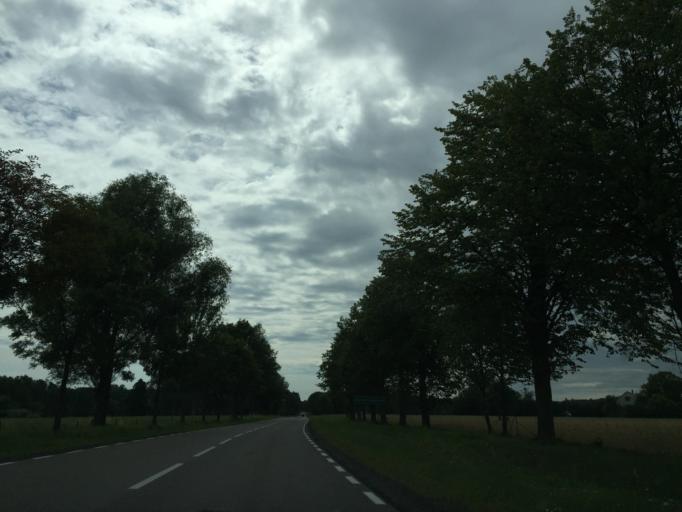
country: PL
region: Podlasie
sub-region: Powiat siemiatycki
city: Dziadkowice
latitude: 52.5992
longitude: 22.9673
